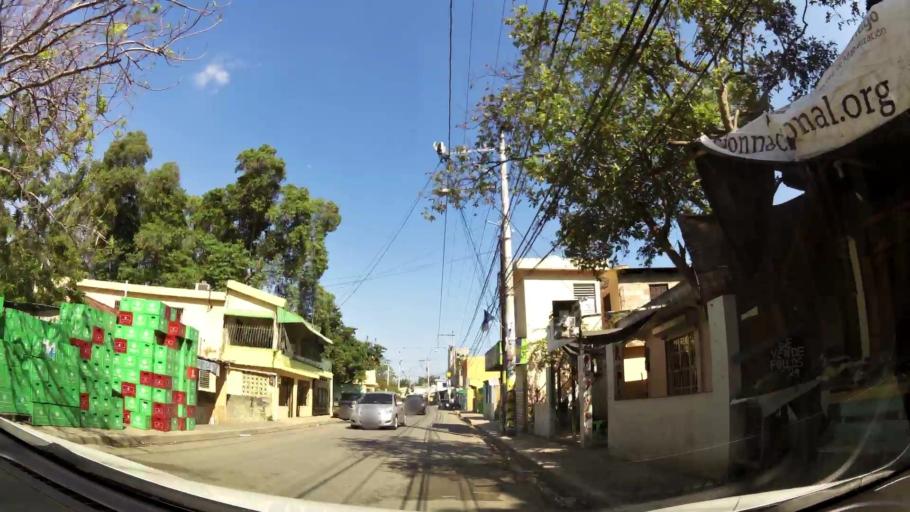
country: DO
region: Santo Domingo
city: Santo Domingo Oeste
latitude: 18.4719
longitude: -70.0027
